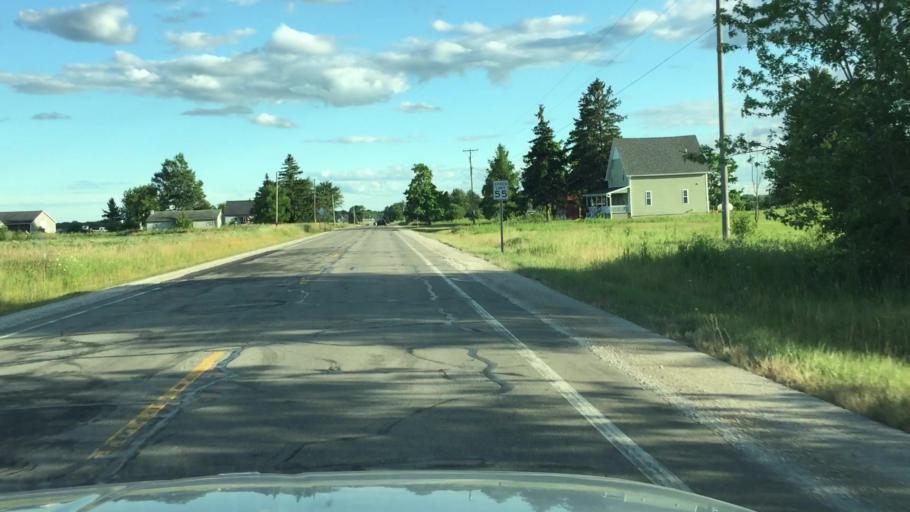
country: US
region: Michigan
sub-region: Saint Clair County
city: Yale
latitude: 43.0867
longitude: -82.7660
